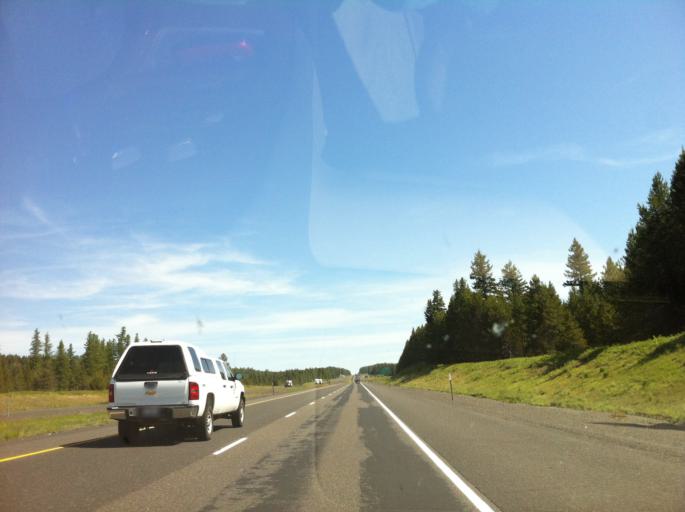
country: US
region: Oregon
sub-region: Umatilla County
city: Mission
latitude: 45.5158
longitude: -118.4348
